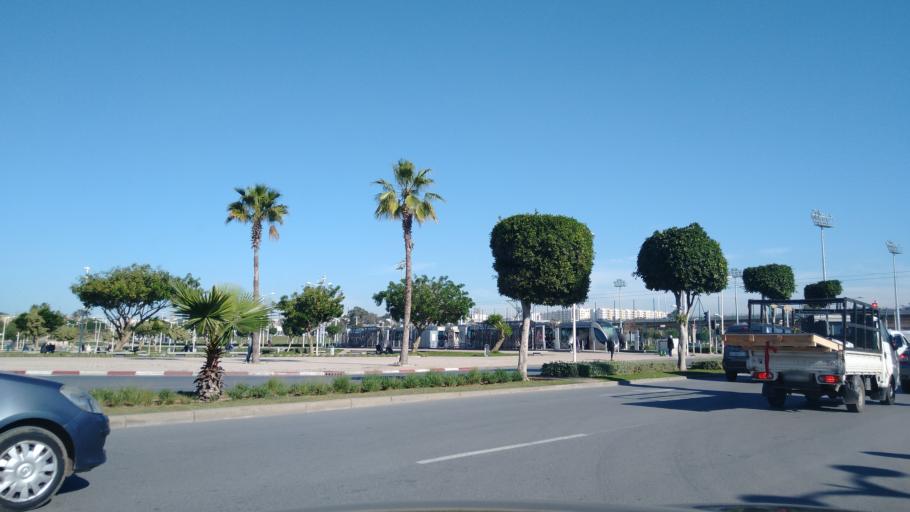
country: MA
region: Rabat-Sale-Zemmour-Zaer
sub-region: Rabat
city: Rabat
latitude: 34.0316
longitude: -6.8203
